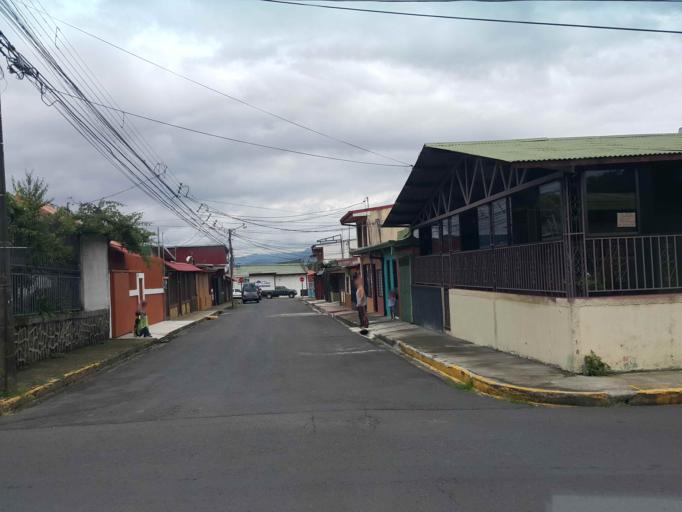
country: CR
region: Heredia
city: Mercedes
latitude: 10.0198
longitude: -84.1222
